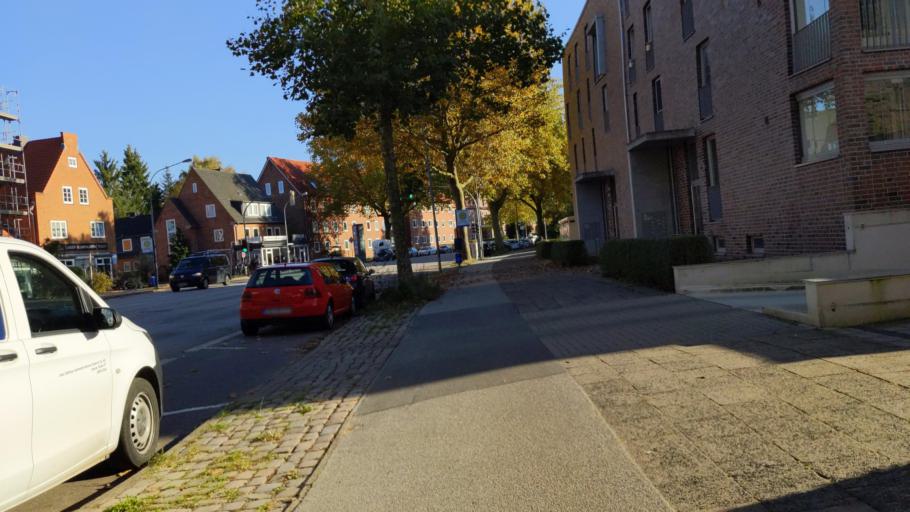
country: DE
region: Schleswig-Holstein
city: Luebeck
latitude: 53.8495
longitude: 10.7052
